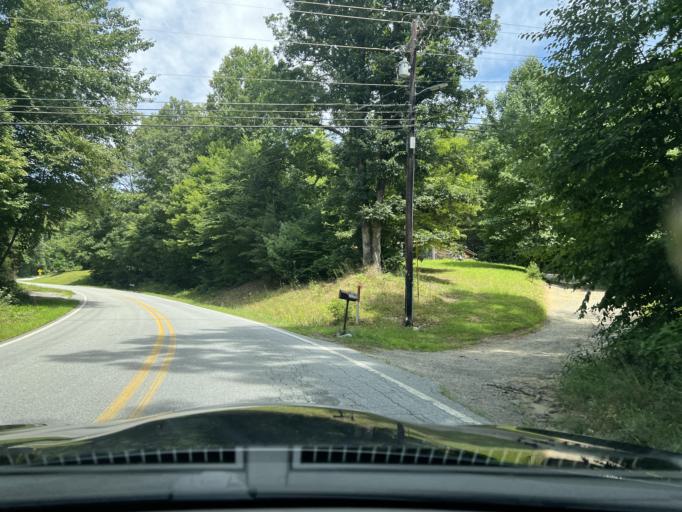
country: US
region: North Carolina
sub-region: Henderson County
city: Edneyville
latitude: 35.3866
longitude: -82.3250
